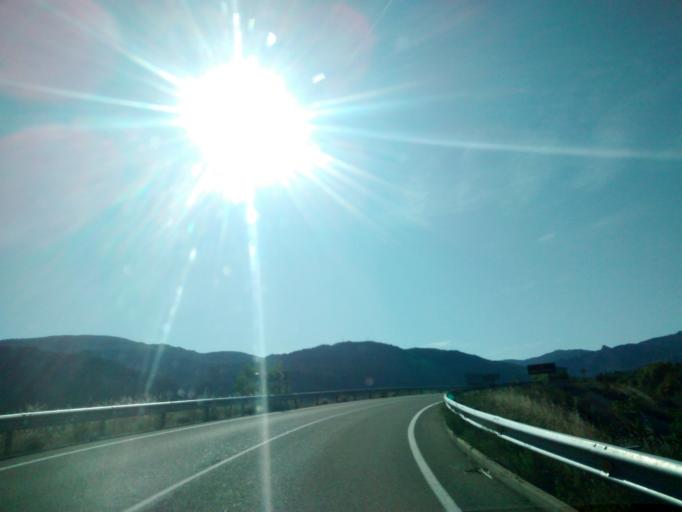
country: ES
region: Aragon
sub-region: Provincia de Huesca
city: Loarre
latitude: 42.3841
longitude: -0.6786
